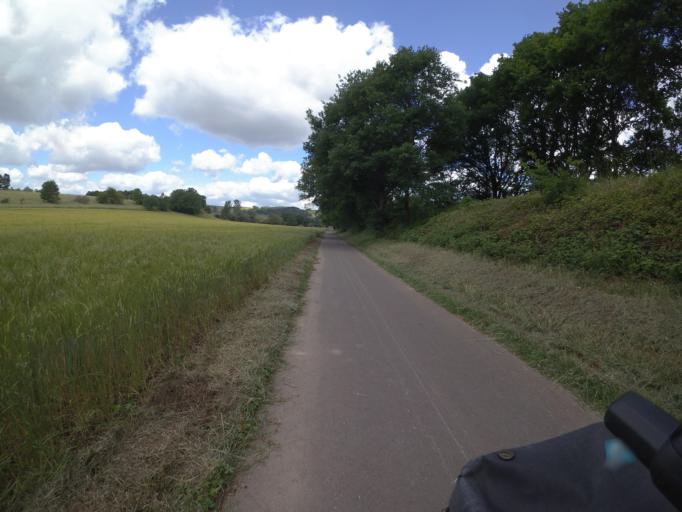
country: DE
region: Rheinland-Pfalz
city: Odernheim
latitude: 49.7796
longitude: 7.7088
